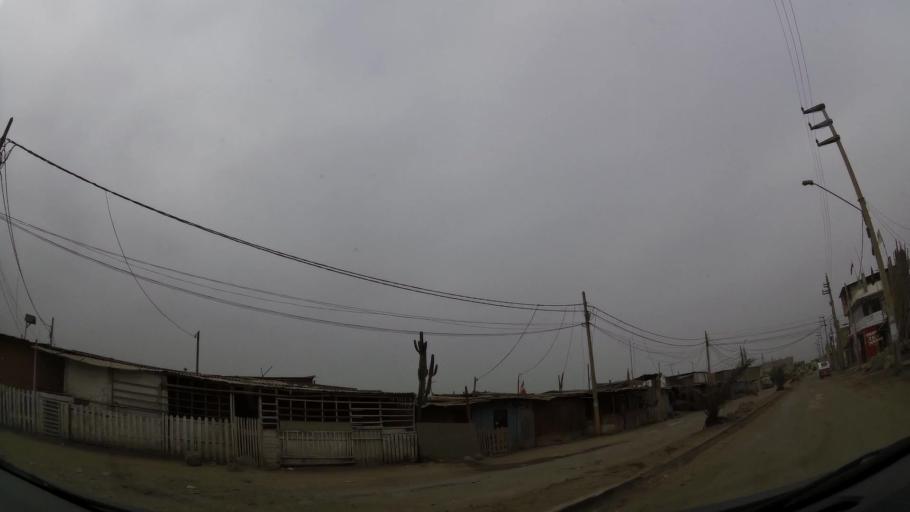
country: PE
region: Lima
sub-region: Lima
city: Surco
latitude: -12.2385
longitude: -76.9306
